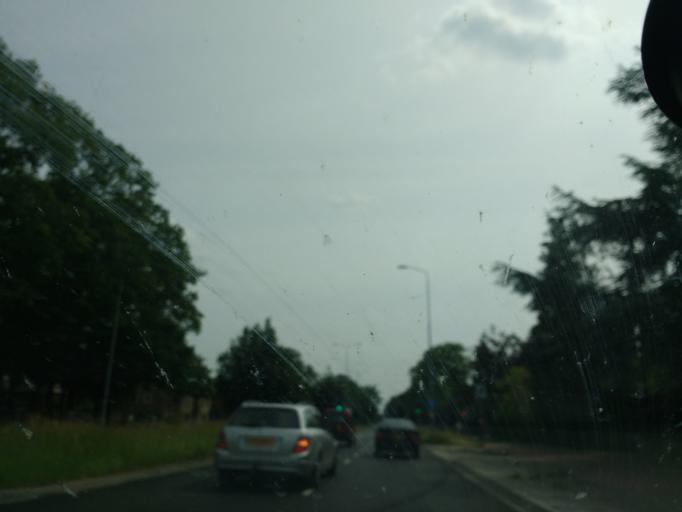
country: NL
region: Gelderland
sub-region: Gemeente Nijmegen
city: Nijmegen
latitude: 51.8172
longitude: 5.8550
